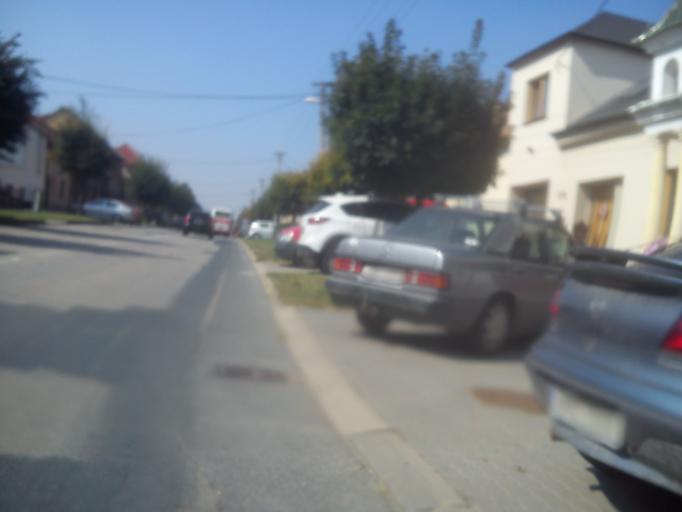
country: CZ
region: South Moravian
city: Sokolnice
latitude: 49.1059
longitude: 16.7519
